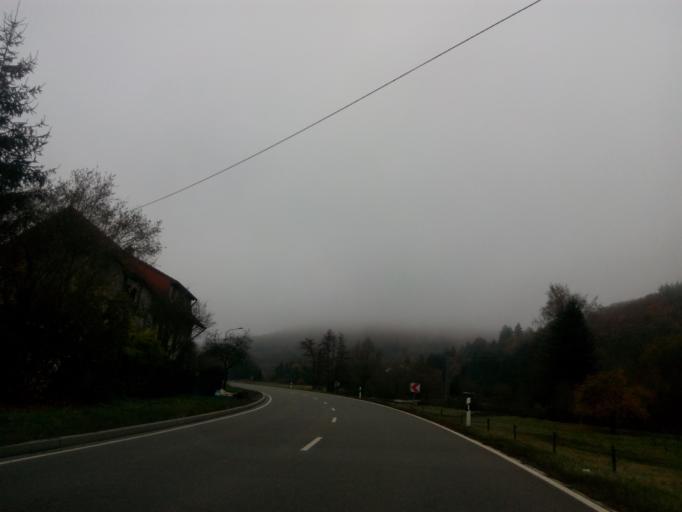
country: DE
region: Rheinland-Pfalz
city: Rutsweiler an der Lauter
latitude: 49.5619
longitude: 7.6227
